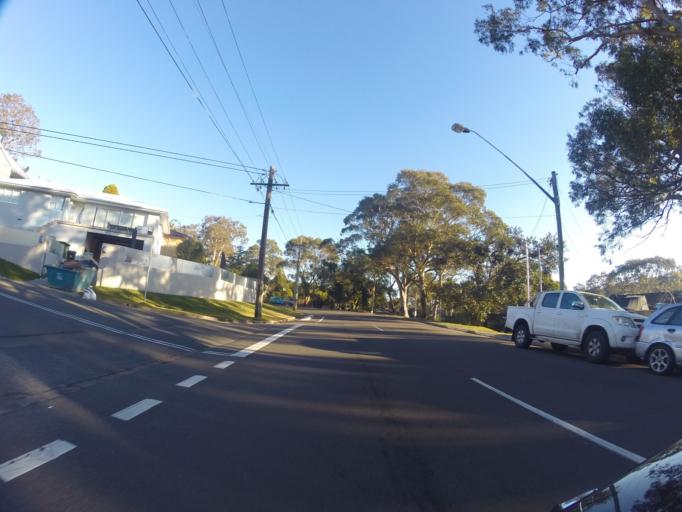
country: AU
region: New South Wales
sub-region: Sutherland Shire
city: Grays Point
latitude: -34.0580
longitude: 151.0808
